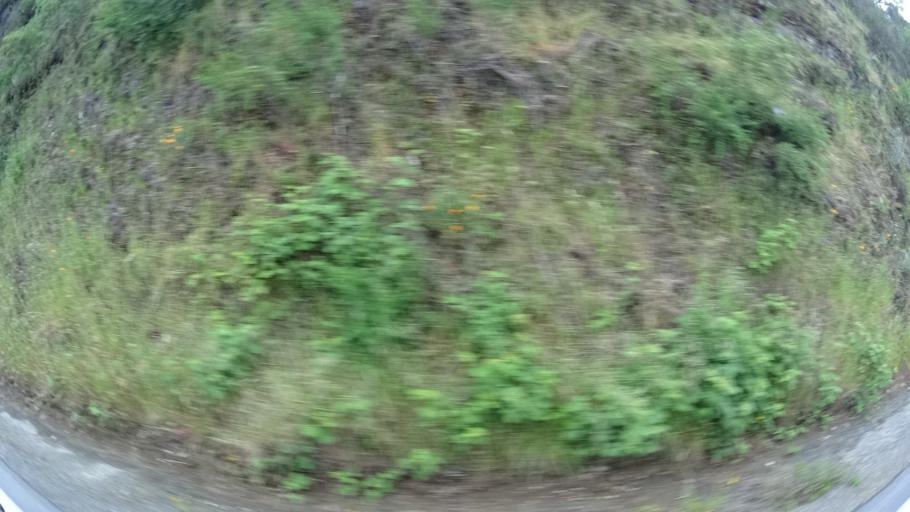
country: US
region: California
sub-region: Humboldt County
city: Willow Creek
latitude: 41.1083
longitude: -123.6866
